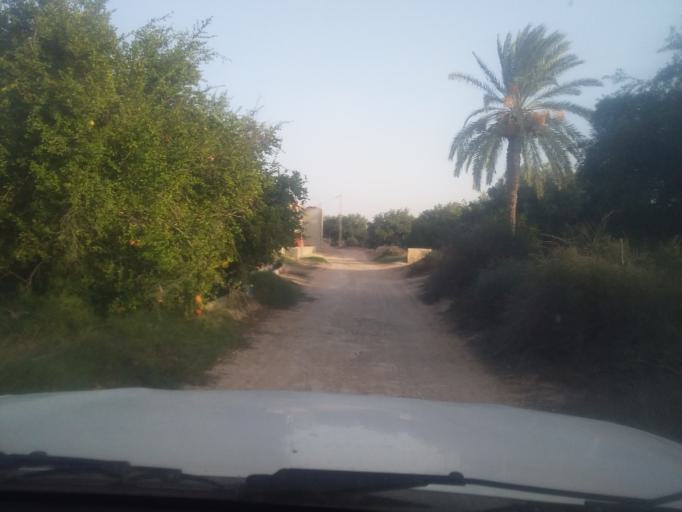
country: TN
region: Qabis
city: Gabes
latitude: 33.6321
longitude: 10.2934
